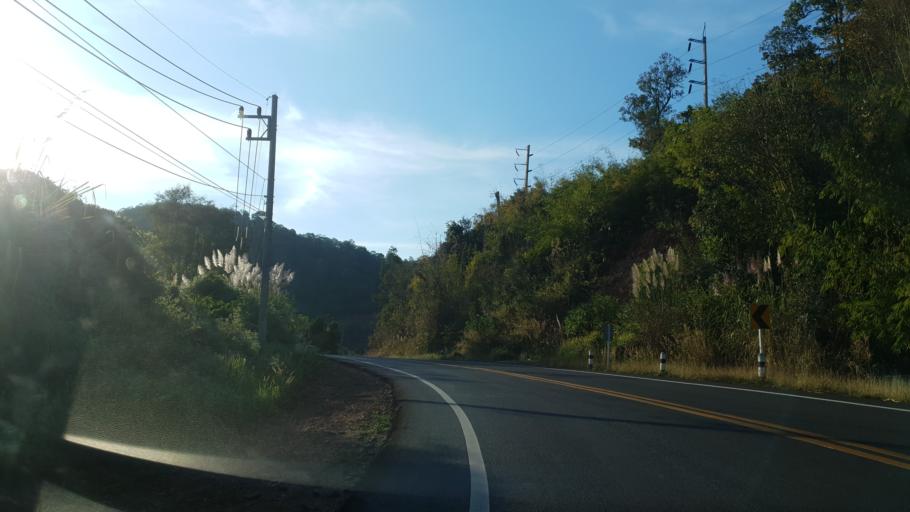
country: TH
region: Loei
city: Dan Sai
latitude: 17.2246
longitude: 101.0659
